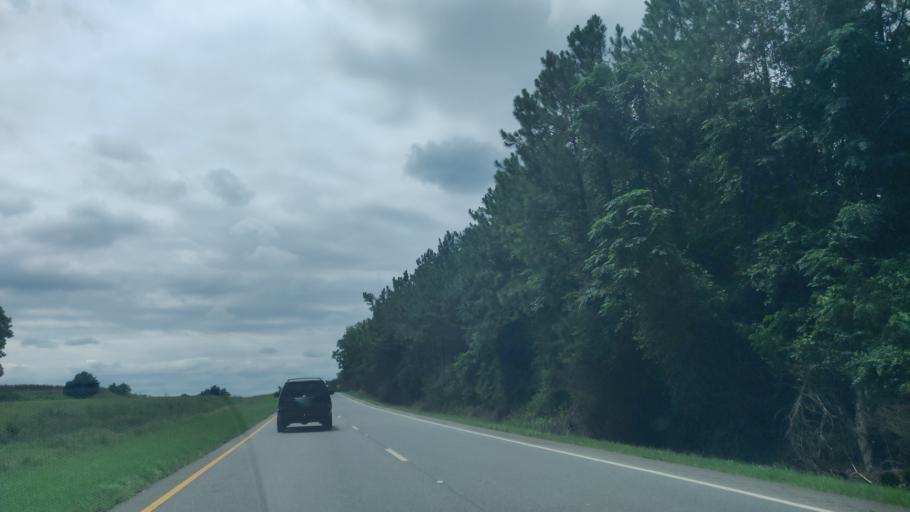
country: US
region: Georgia
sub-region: Terrell County
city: Dawson
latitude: 31.8646
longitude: -84.4842
